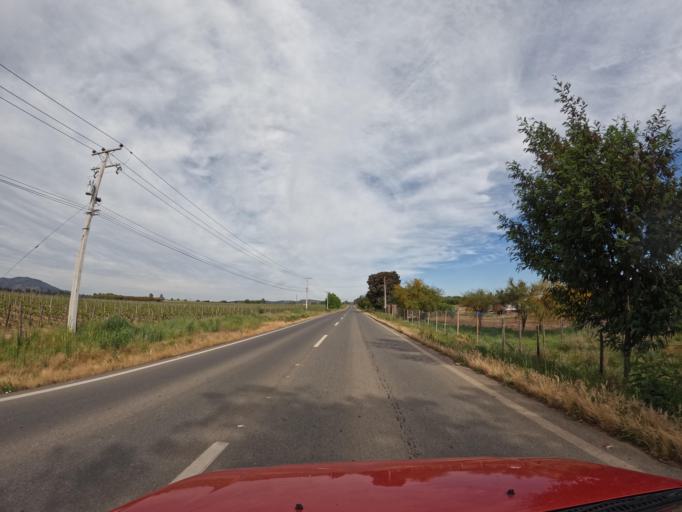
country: CL
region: Maule
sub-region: Provincia de Talca
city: Talca
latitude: -35.3821
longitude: -71.8238
